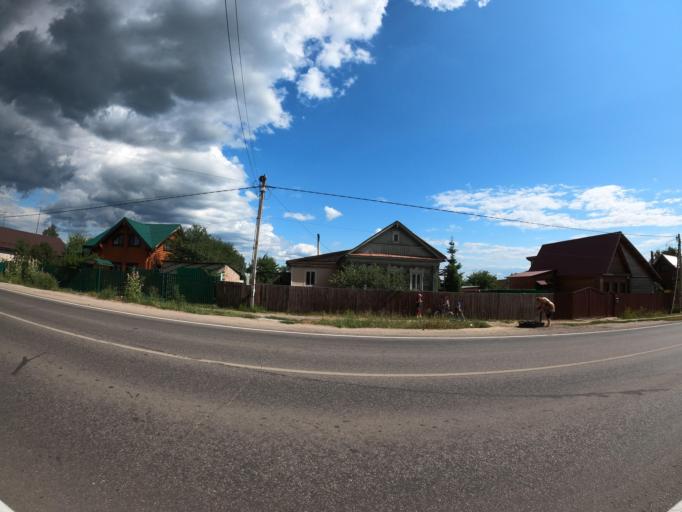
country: RU
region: Moskovskaya
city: Konobeyevo
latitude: 55.4083
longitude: 38.6608
